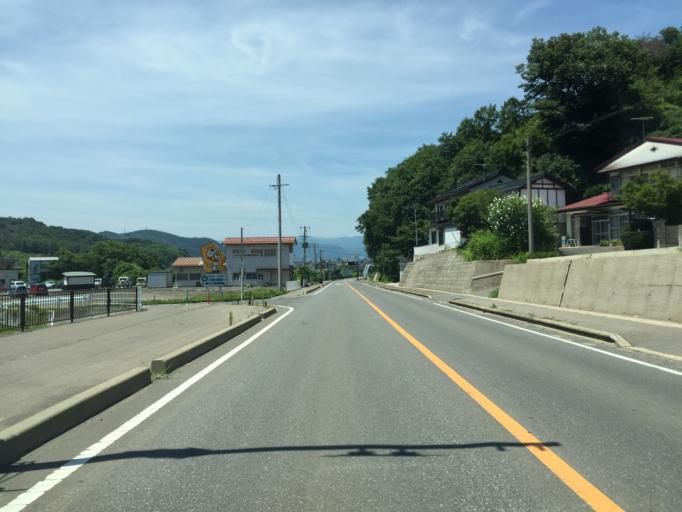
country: JP
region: Fukushima
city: Fukushima-shi
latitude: 37.7675
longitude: 140.5147
